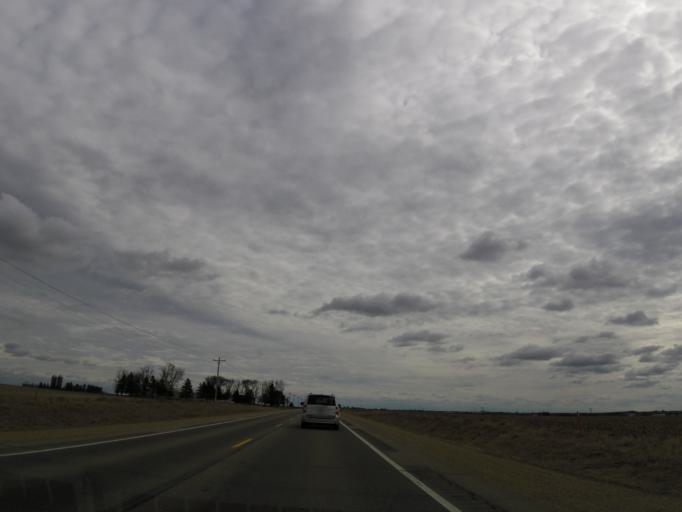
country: US
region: Iowa
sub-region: Chickasaw County
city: New Hampton
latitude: 43.1324
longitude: -92.2984
